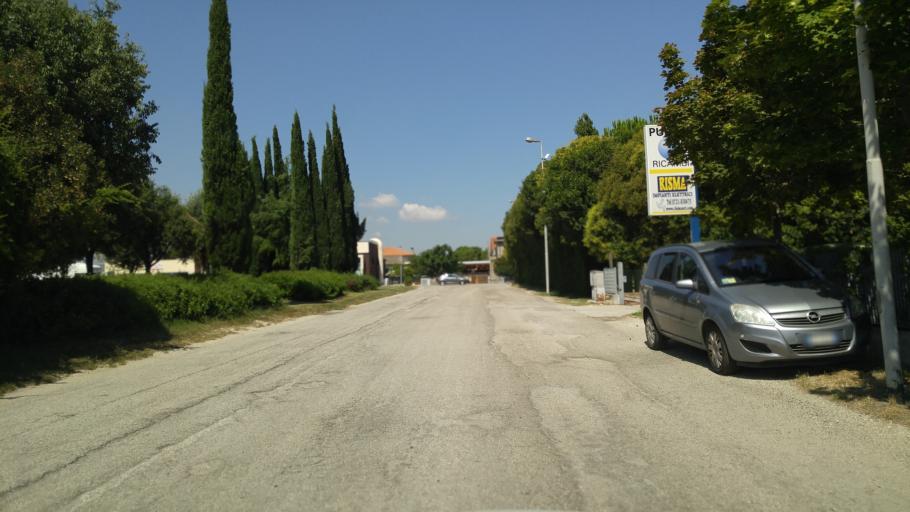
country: IT
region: The Marches
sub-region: Provincia di Pesaro e Urbino
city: Fano
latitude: 43.8252
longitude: 13.0411
